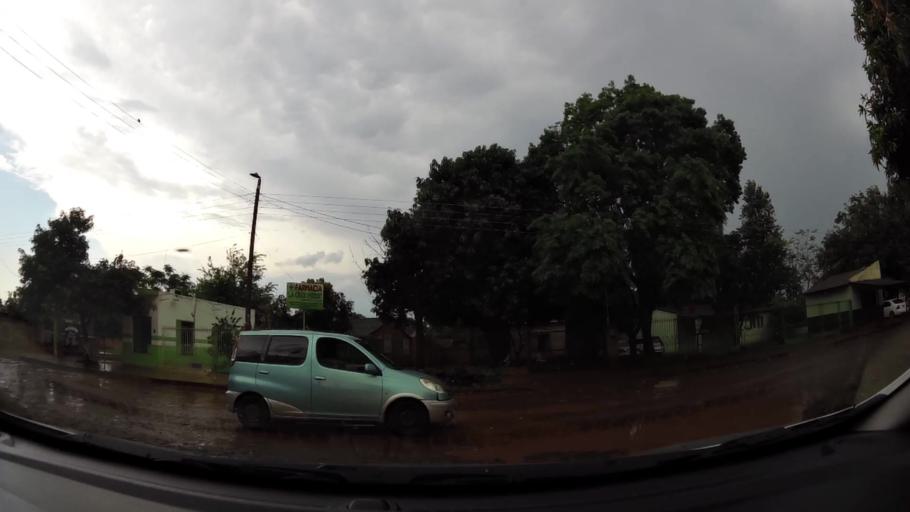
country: PY
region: Alto Parana
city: Presidente Franco
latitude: -25.5375
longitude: -54.6556
